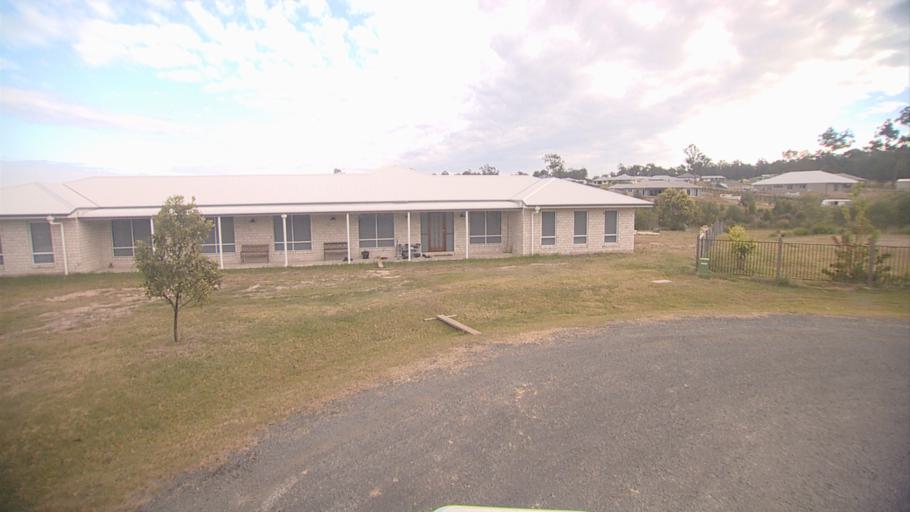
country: AU
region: Queensland
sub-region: Logan
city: Logan Reserve
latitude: -27.7507
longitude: 153.1401
